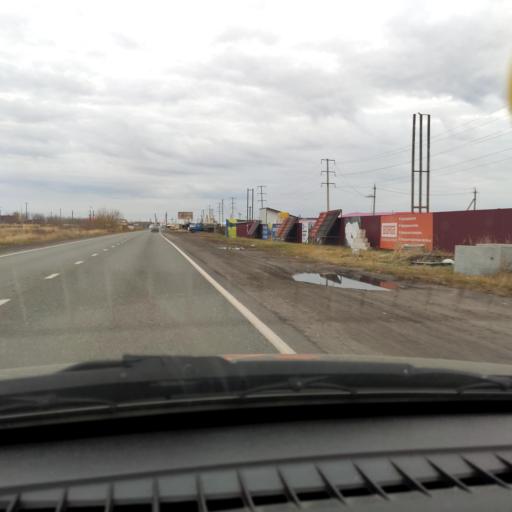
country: RU
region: Samara
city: Podstepki
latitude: 53.5220
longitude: 49.2004
